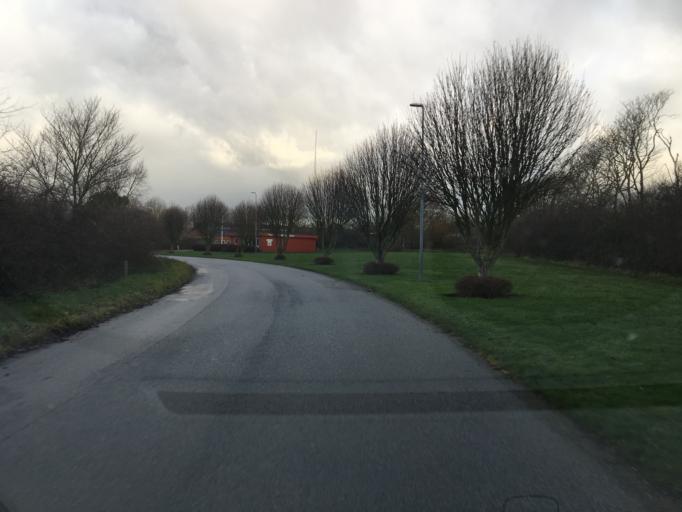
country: DK
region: South Denmark
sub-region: Tonder Kommune
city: Sherrebek
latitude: 55.1561
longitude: 8.7790
